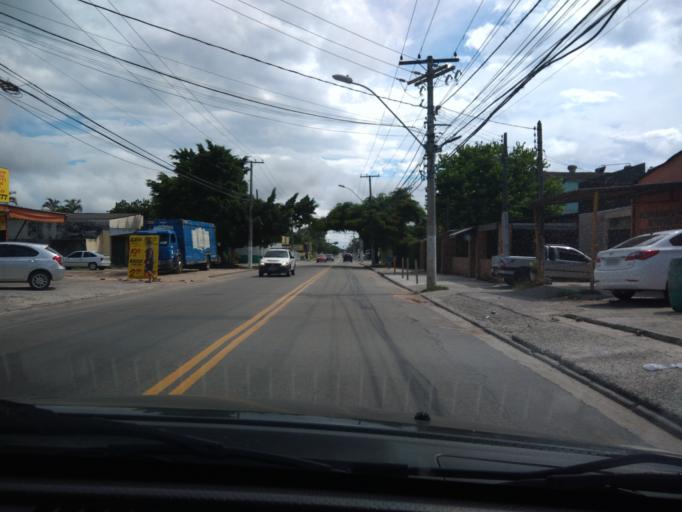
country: BR
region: Rio de Janeiro
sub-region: Niteroi
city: Niteroi
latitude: -22.9295
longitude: -43.0149
